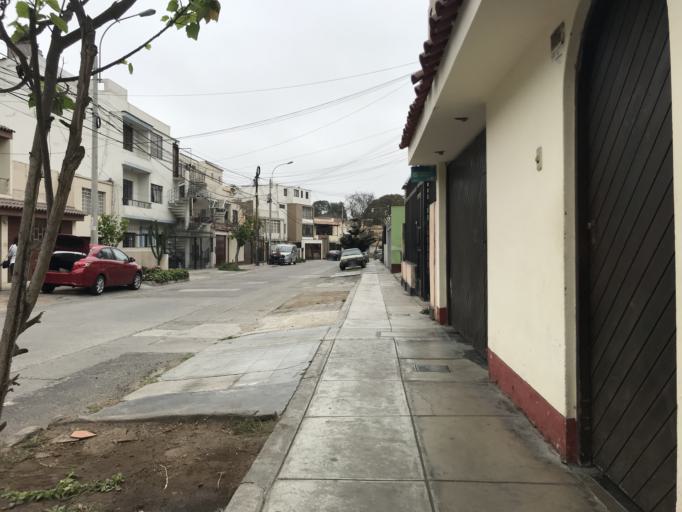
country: PE
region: Lima
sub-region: Lima
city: San Isidro
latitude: -12.0808
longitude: -77.0674
